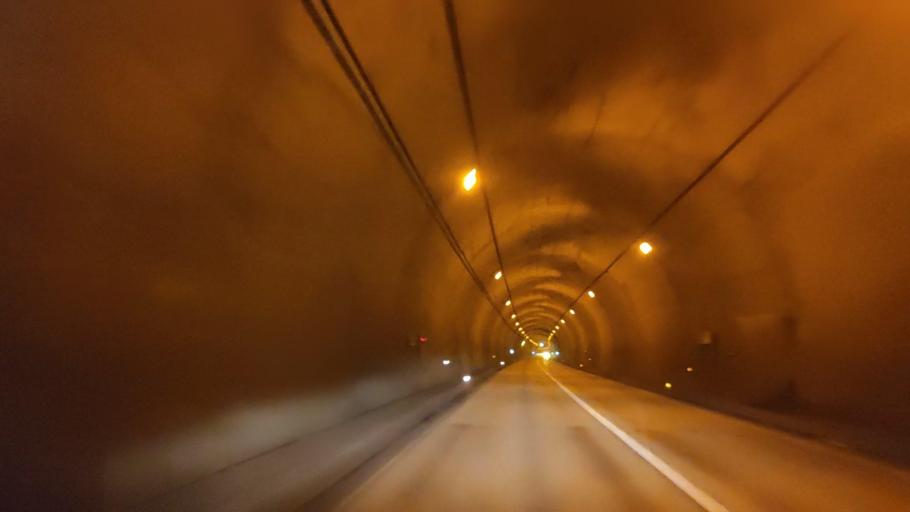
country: JP
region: Tottori
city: Kurayoshi
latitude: 35.3110
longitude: 133.7505
